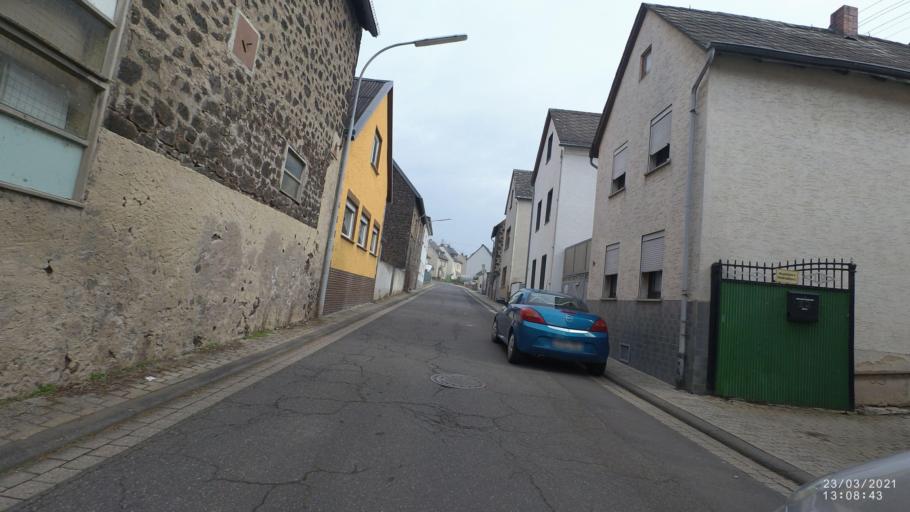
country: DE
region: Rheinland-Pfalz
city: Ochtendung
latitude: 50.3475
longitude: 7.3933
